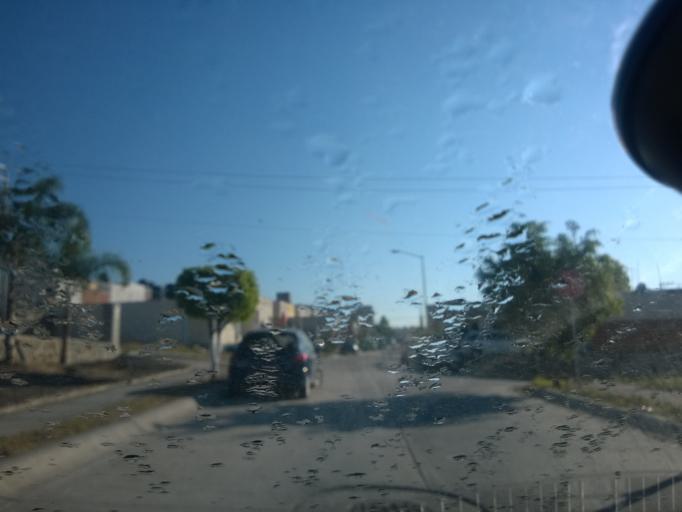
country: MX
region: Guanajuato
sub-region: Leon
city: La Ermita
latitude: 21.1566
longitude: -101.7463
